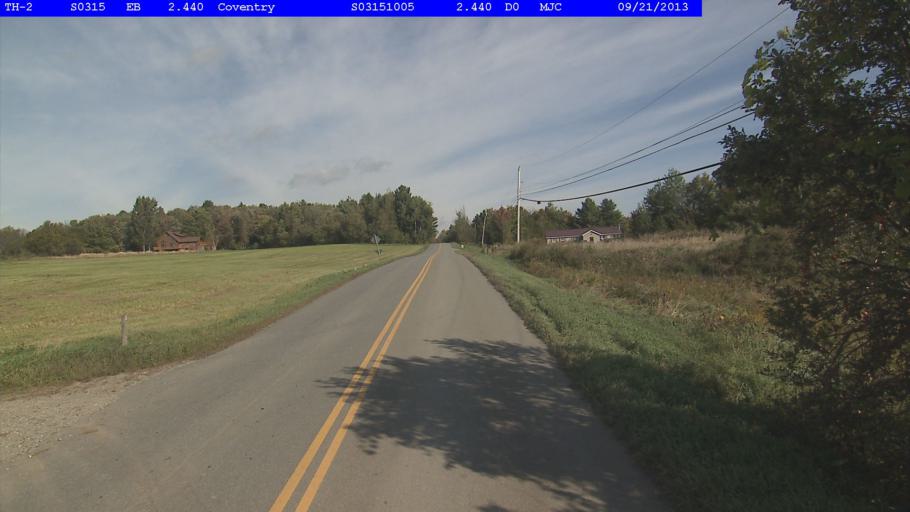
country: US
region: Vermont
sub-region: Orleans County
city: Newport
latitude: 44.8714
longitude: -72.2145
